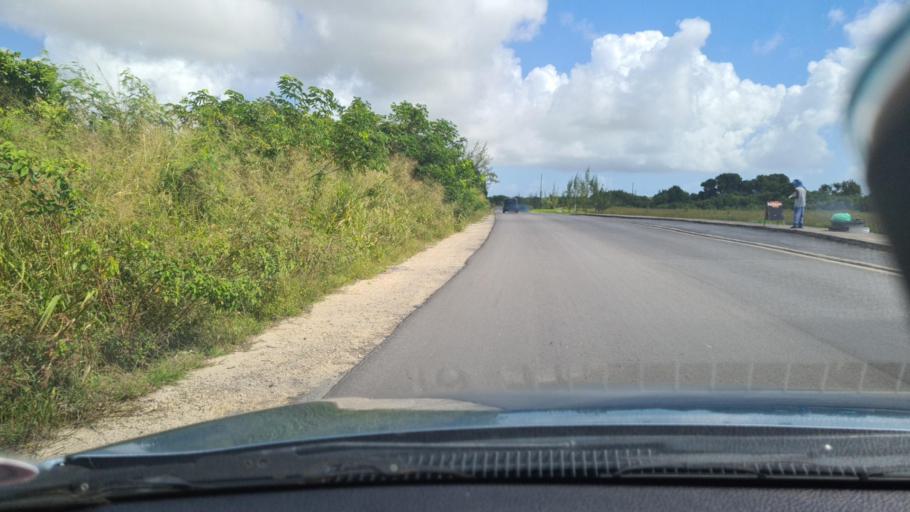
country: BB
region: Christ Church
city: Oistins
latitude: 13.0883
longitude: -59.5181
